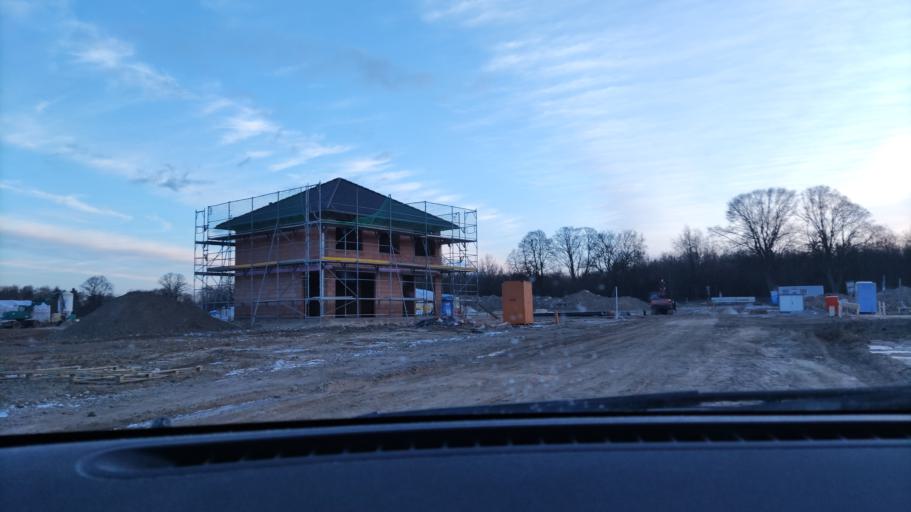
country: DE
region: Schleswig-Holstein
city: Kruzen
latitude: 53.3759
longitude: 10.5252
